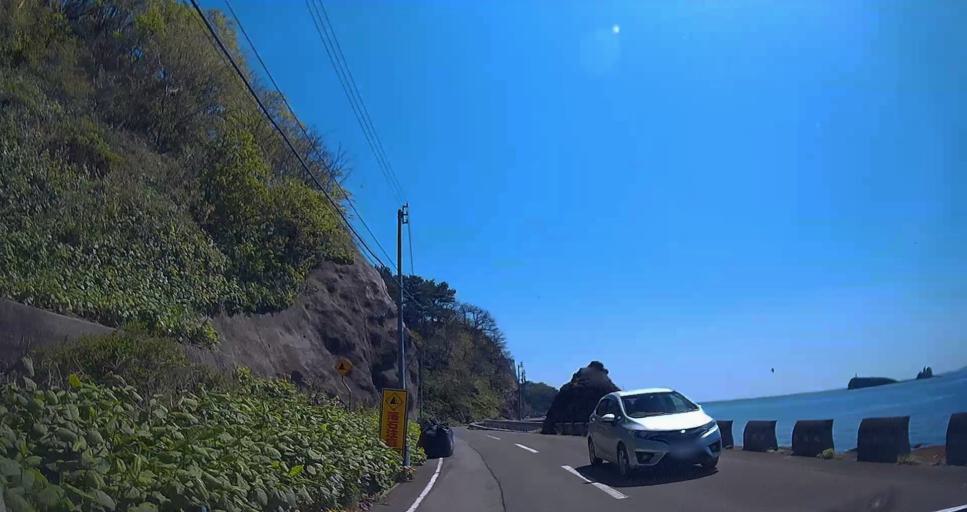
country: JP
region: Aomori
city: Aomori Shi
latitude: 41.1288
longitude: 140.8025
